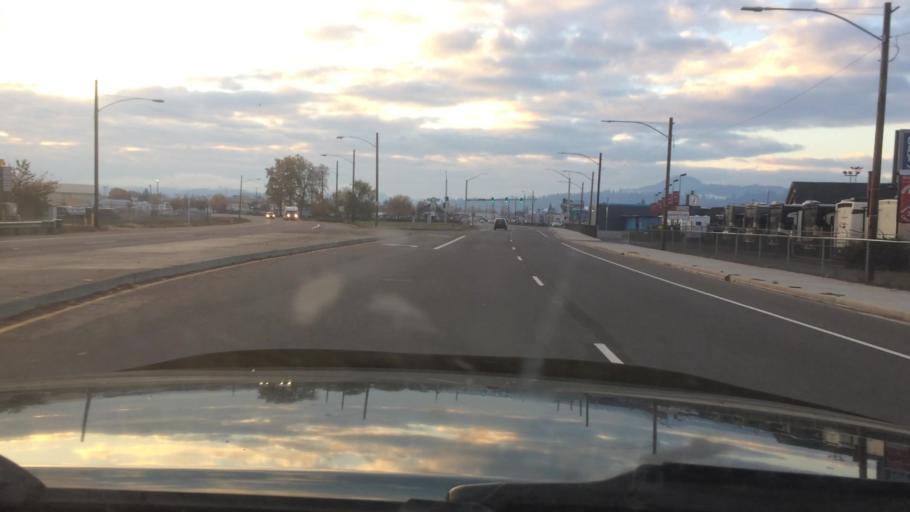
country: US
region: Oregon
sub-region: Lane County
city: Eugene
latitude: 44.0565
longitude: -123.1301
